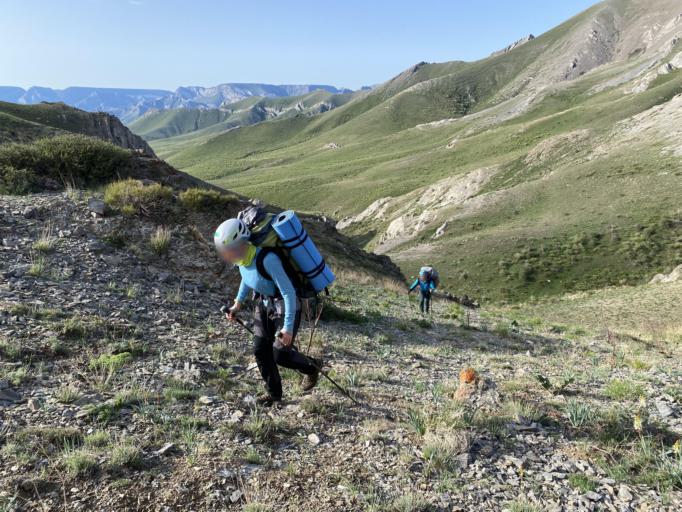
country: KZ
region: Ongtustik Qazaqstan
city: Ashchysay
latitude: 43.7616
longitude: 68.8021
